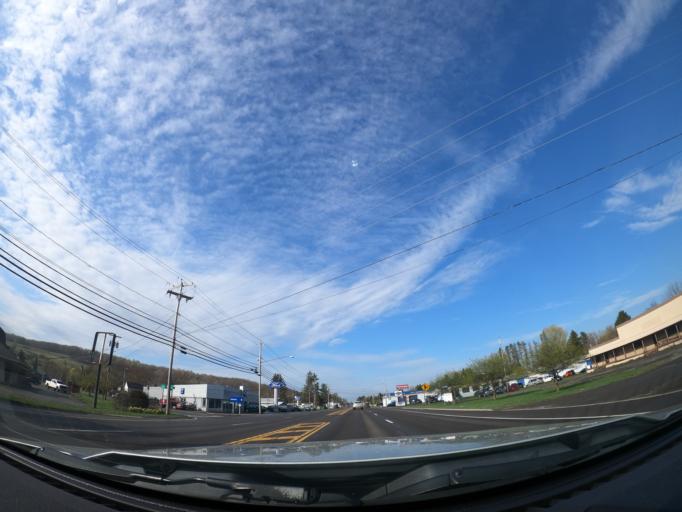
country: US
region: New York
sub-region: Cortland County
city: Munsons Corners
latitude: 42.5850
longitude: -76.2010
